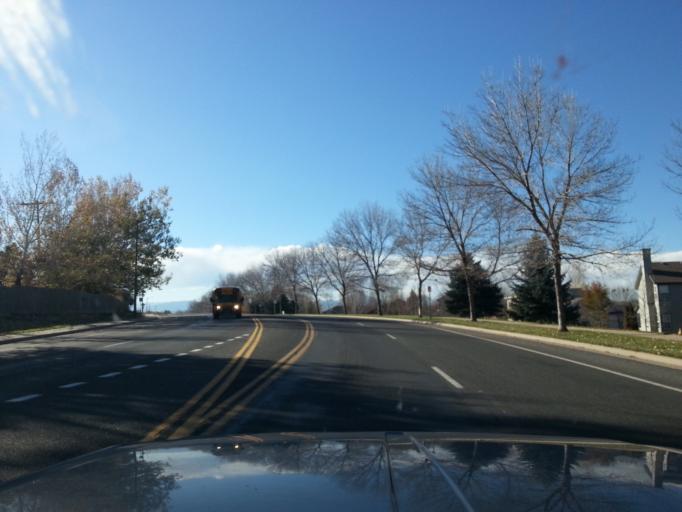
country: US
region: Colorado
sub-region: Larimer County
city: Loveland
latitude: 40.3929
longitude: -105.1021
